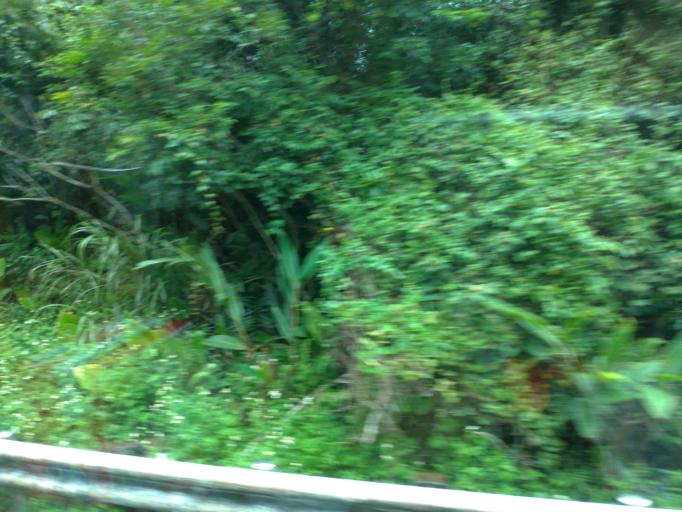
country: TW
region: Taiwan
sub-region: Keelung
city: Keelung
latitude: 25.1131
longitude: 121.7291
